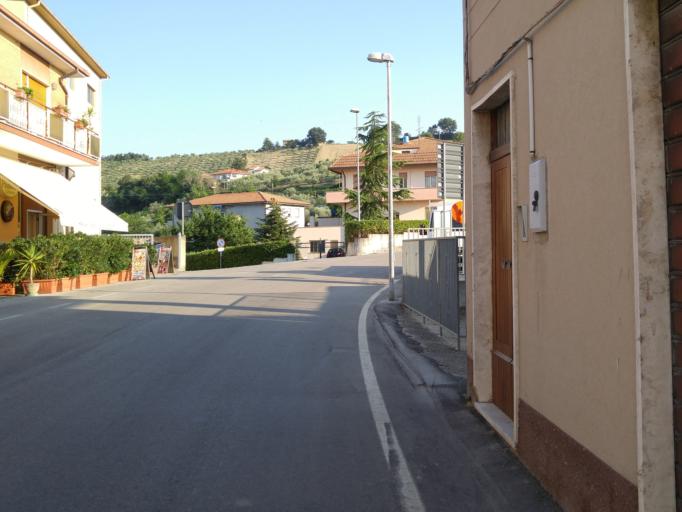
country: IT
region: Abruzzo
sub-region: Provincia di Teramo
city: Castilenti
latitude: 42.5591
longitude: 13.9223
